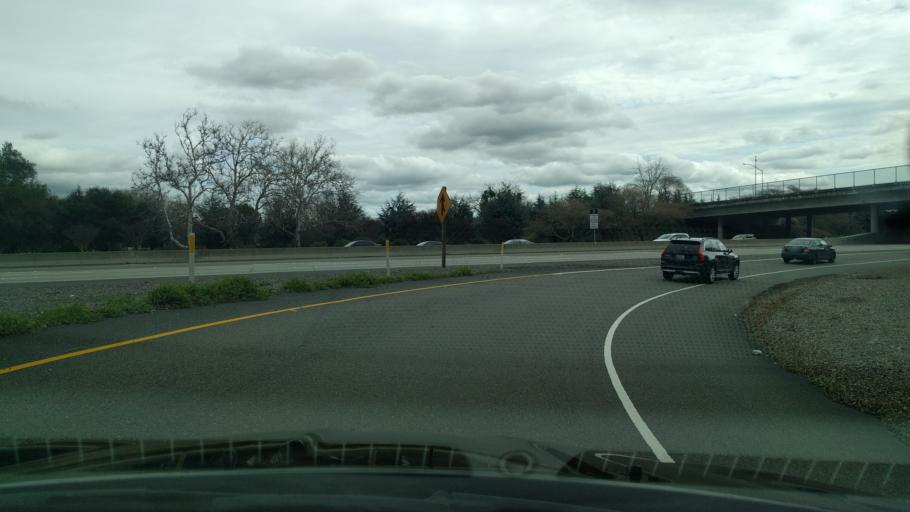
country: US
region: California
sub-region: Contra Costa County
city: San Ramon
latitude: 37.7607
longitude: -121.9665
